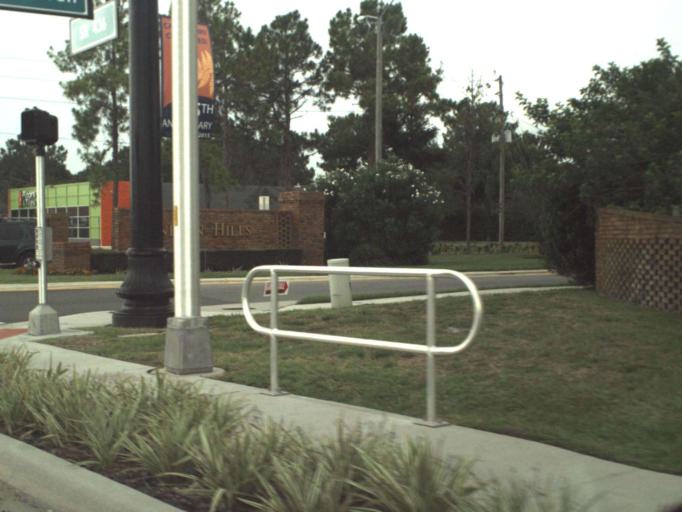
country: US
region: Florida
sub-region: Seminole County
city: Fern Park
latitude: 28.6489
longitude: -81.3255
